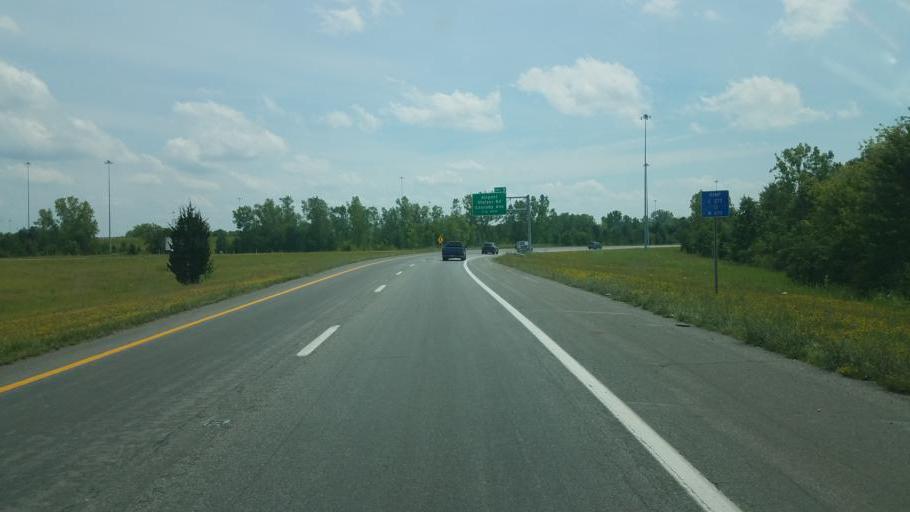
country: US
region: Ohio
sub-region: Franklin County
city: Gahanna
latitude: 40.0153
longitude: -82.9060
